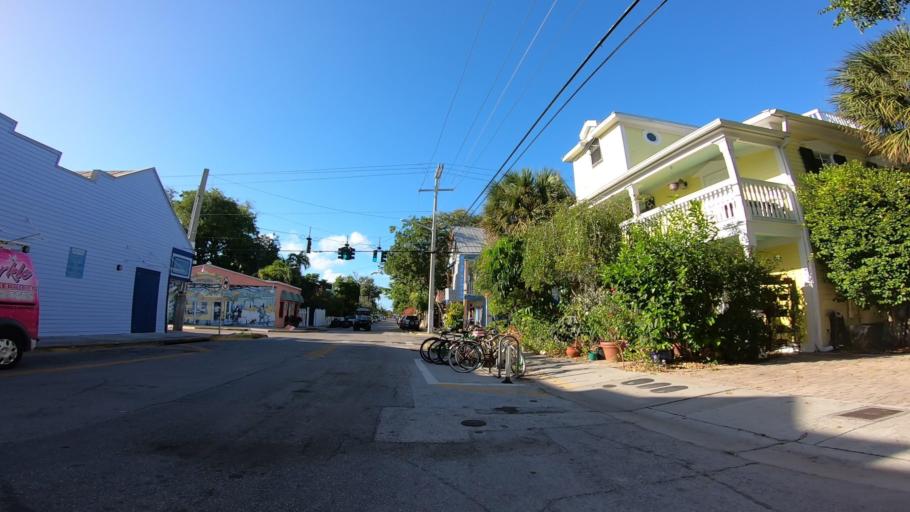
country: US
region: Florida
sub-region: Monroe County
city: Key West
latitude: 24.5515
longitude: -81.8027
